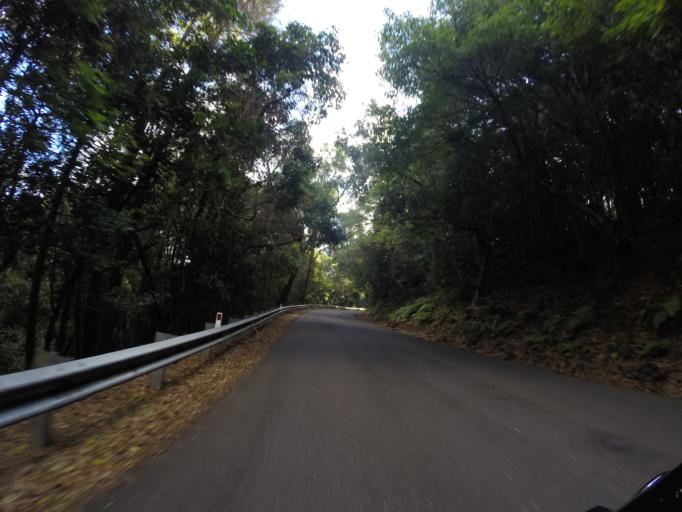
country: AU
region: New South Wales
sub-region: Wollongong
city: Mount Keira
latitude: -34.3981
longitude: 150.8511
